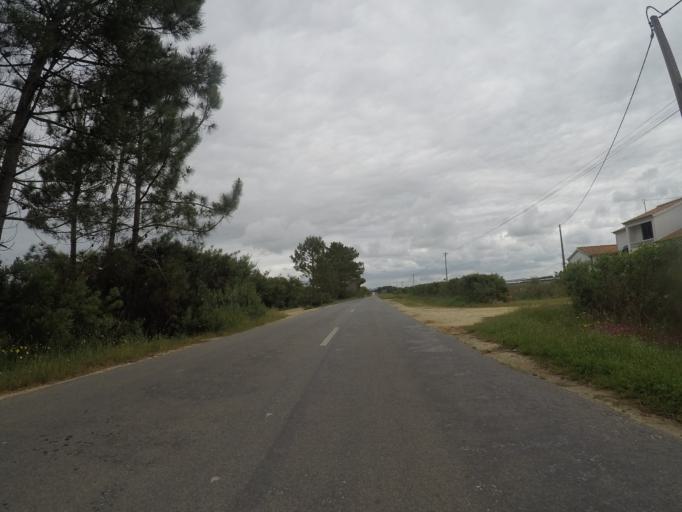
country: PT
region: Beja
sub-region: Odemira
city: Vila Nova de Milfontes
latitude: 37.6084
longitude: -8.7967
